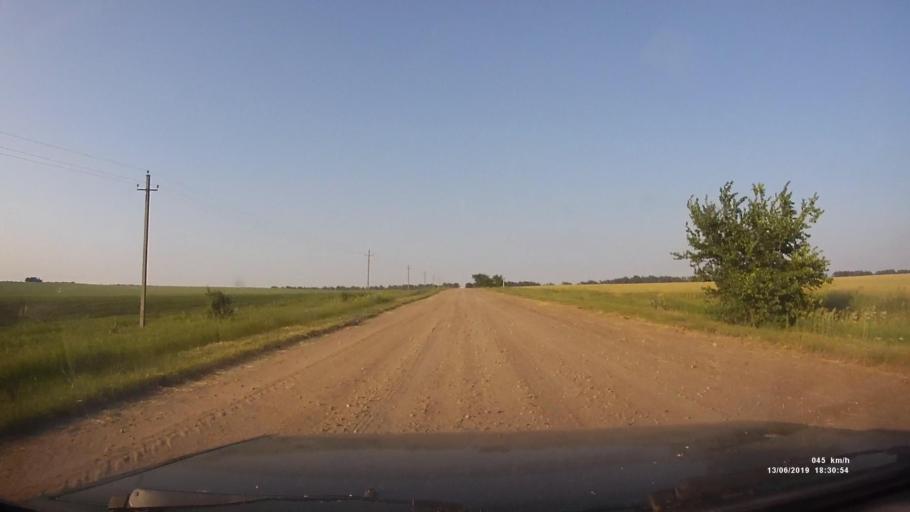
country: RU
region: Rostov
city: Kazanskaya
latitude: 49.8639
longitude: 41.3542
